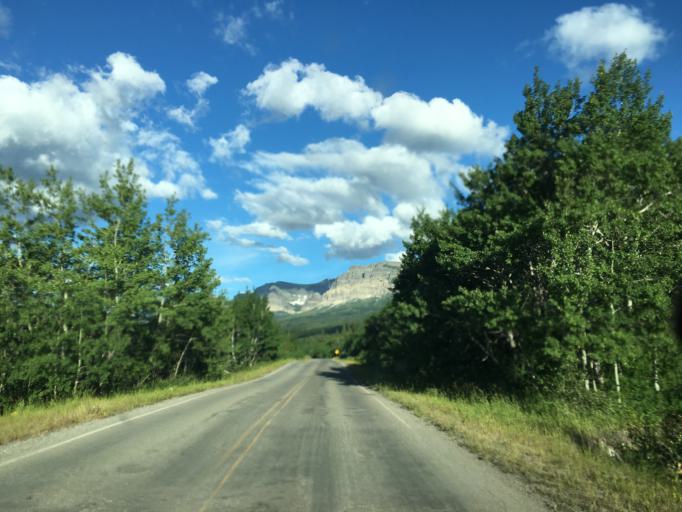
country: CA
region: Alberta
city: Cardston
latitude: 48.8301
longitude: -113.5284
